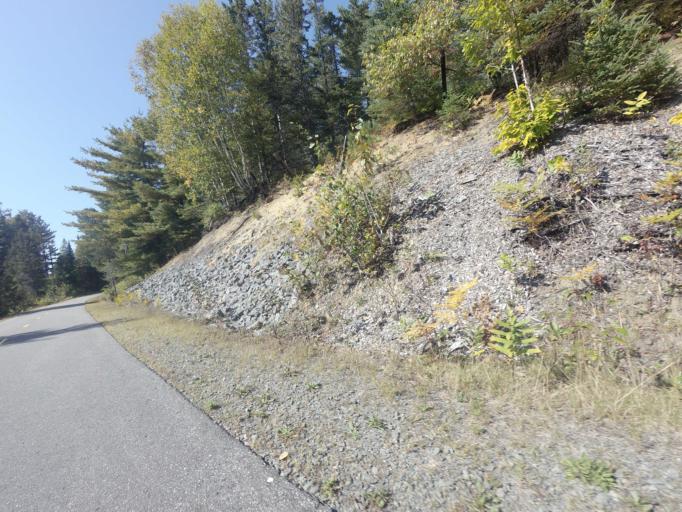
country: CA
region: Quebec
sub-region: Laurentides
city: Mont-Tremblant
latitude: 46.1287
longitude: -74.5769
